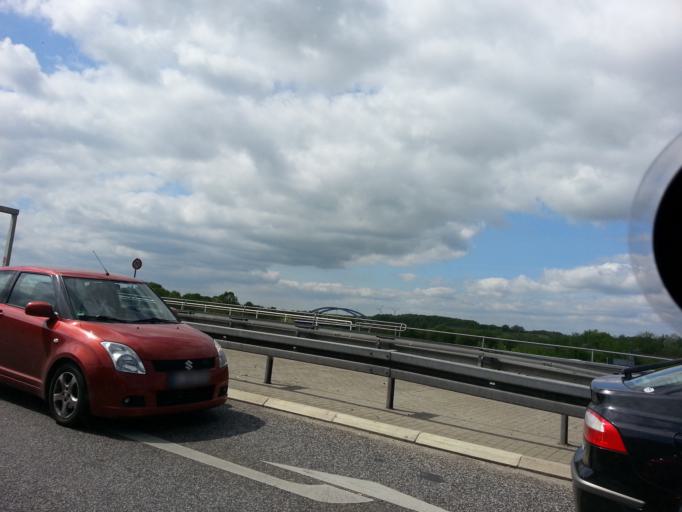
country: DE
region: Brandenburg
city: Ahrensfelde
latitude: 52.6019
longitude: 13.6086
